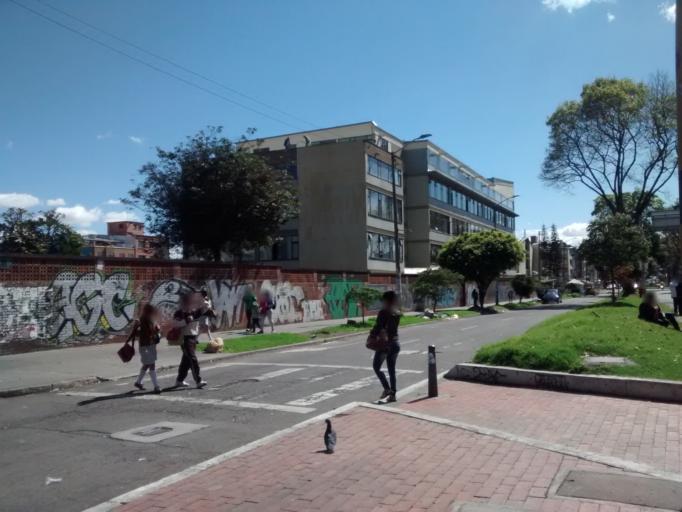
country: CO
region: Bogota D.C.
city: Bogota
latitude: 4.6339
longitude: -74.0757
